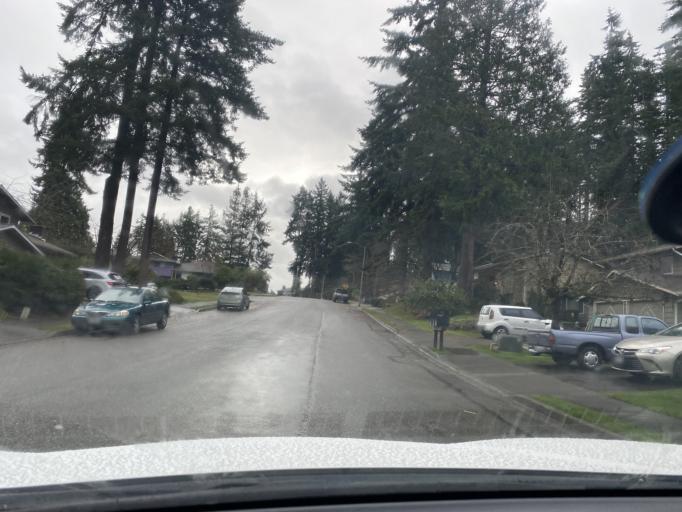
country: US
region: Washington
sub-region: Snohomish County
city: Lynnwood
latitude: 47.8413
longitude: -122.3141
